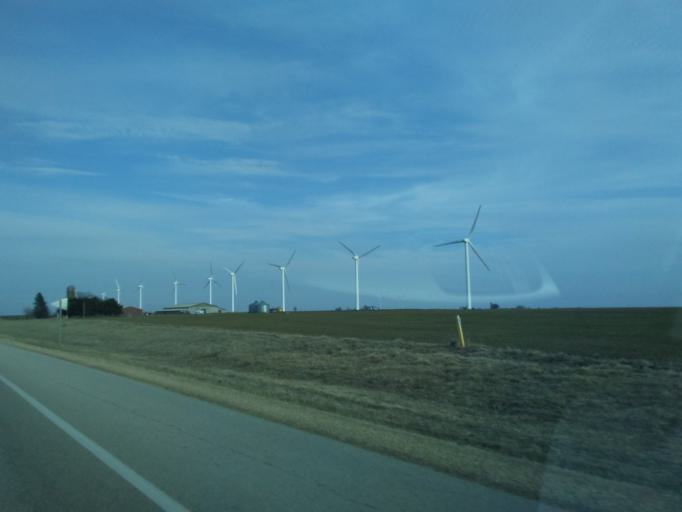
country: US
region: Wisconsin
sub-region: Grant County
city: Muscoda
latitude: 42.9664
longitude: -90.3944
